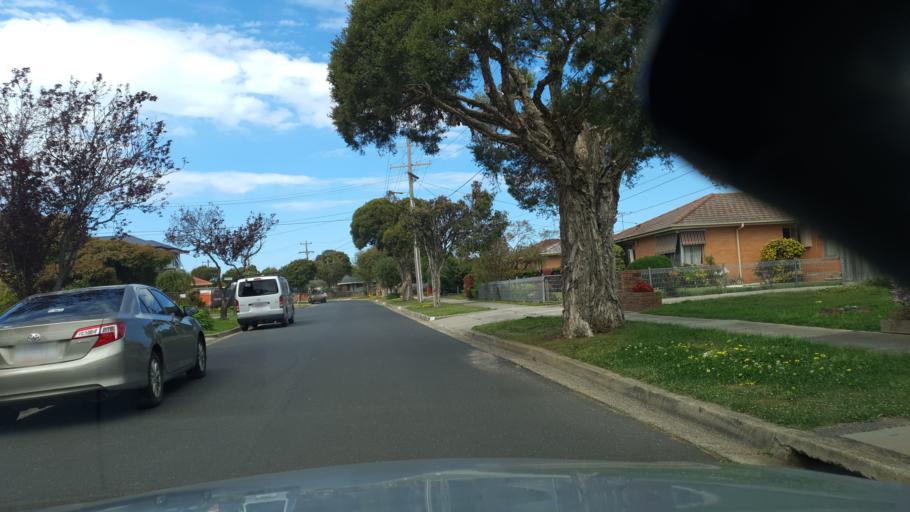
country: AU
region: Victoria
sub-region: Greater Dandenong
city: Springvale
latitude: -37.9267
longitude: 145.1686
